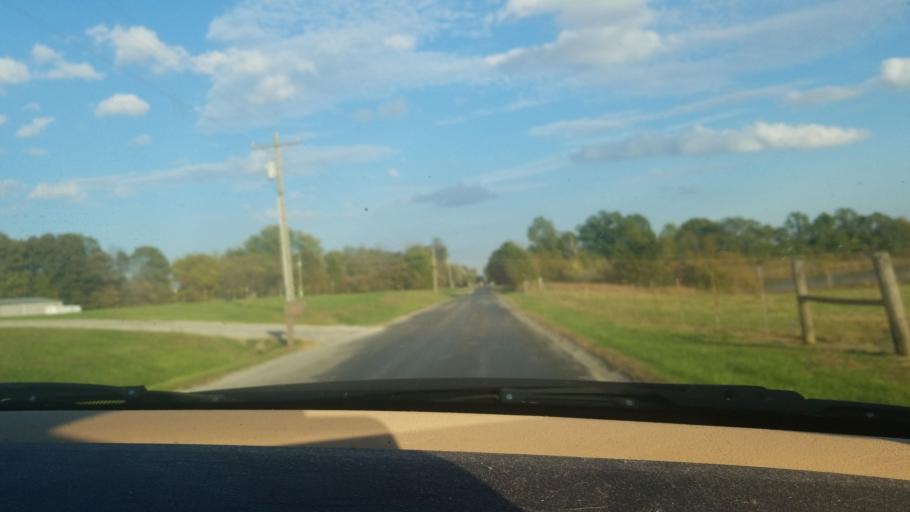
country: US
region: Illinois
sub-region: Saline County
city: Carrier Mills
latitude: 37.7719
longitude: -88.7370
